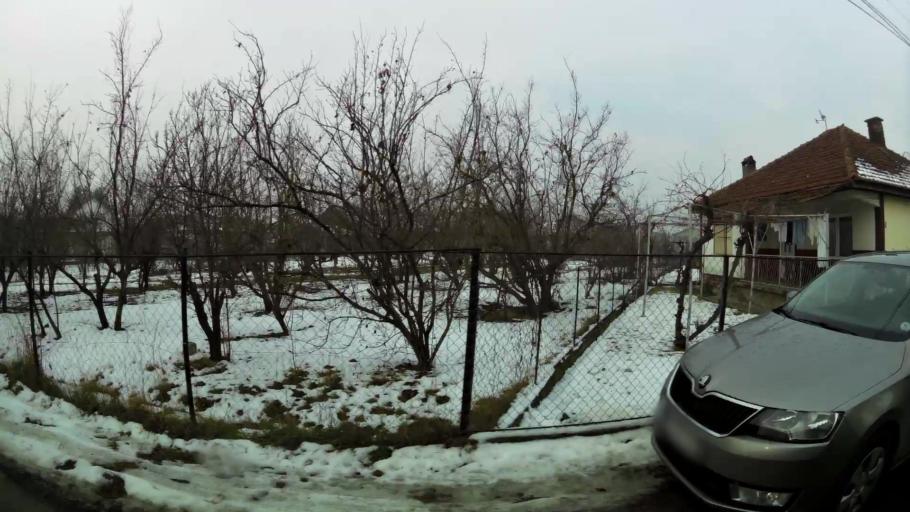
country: MK
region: Ilinden
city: Jurumleri
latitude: 41.9683
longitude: 21.5607
